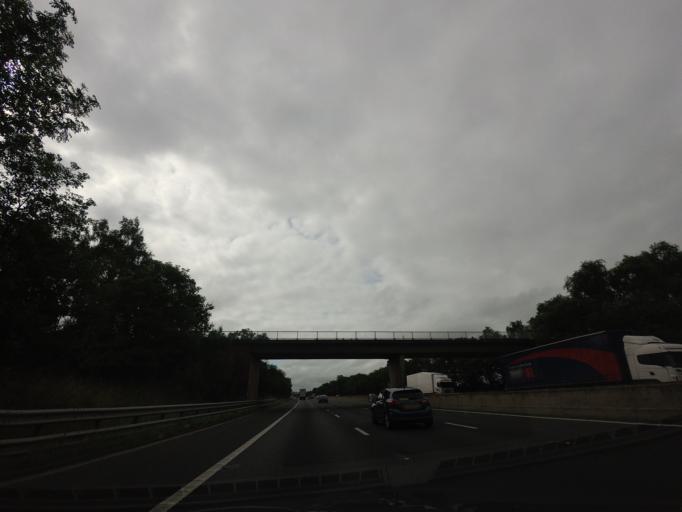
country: GB
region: England
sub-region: Cumbria
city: Scotby
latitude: 54.8263
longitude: -2.8891
